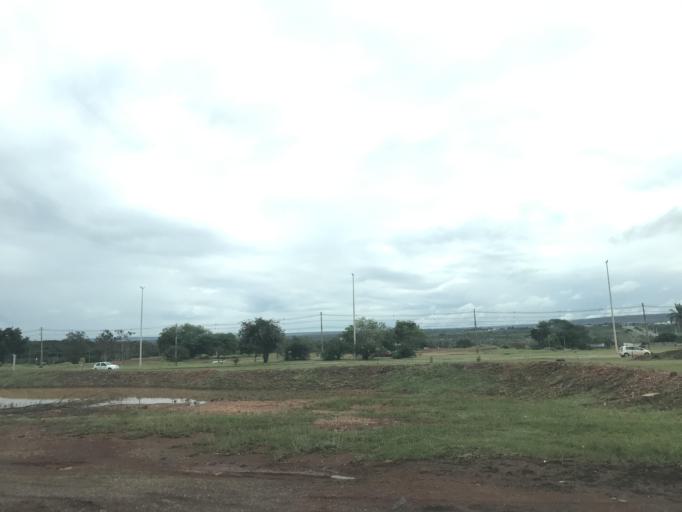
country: BR
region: Federal District
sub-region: Brasilia
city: Brasilia
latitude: -15.7387
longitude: -47.9107
